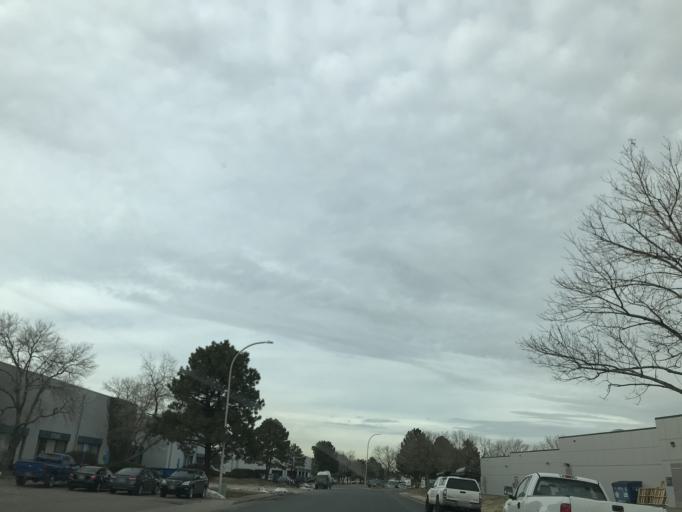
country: US
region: Colorado
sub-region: Adams County
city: Commerce City
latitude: 39.7812
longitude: -104.9085
